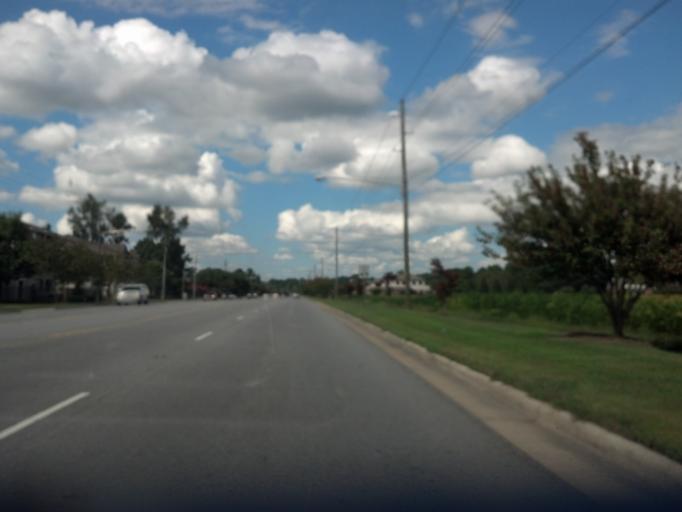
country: US
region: North Carolina
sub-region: Pitt County
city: Windsor
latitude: 35.5725
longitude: -77.3531
